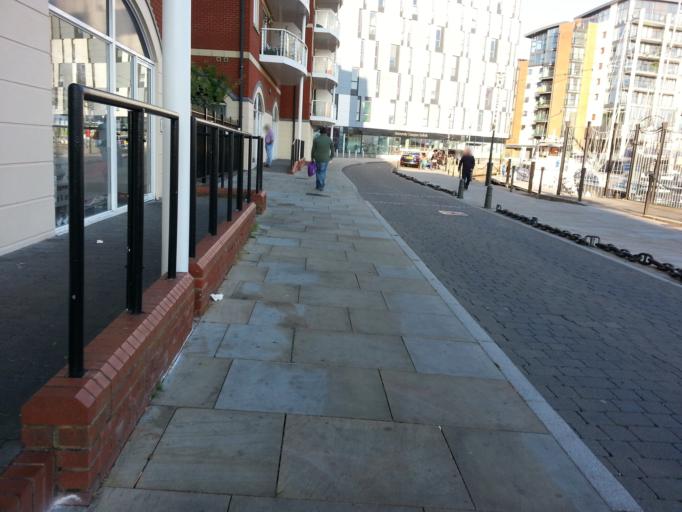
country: GB
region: England
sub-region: Suffolk
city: Ipswich
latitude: 52.0526
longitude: 1.1620
